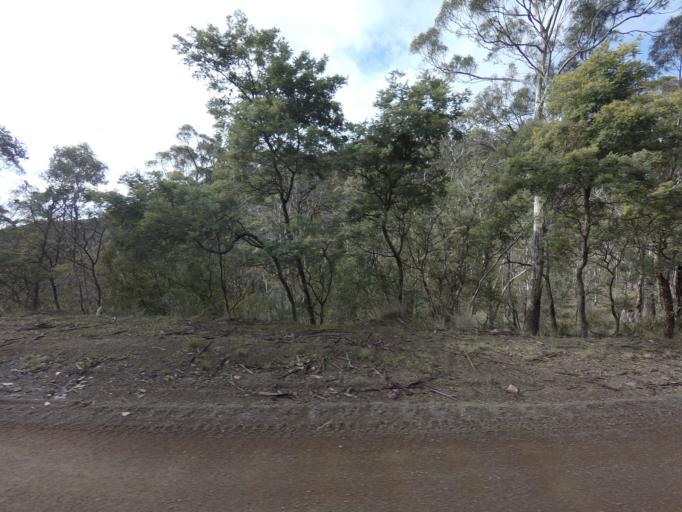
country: AU
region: Tasmania
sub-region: Derwent Valley
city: New Norfolk
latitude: -42.7441
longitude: 146.8673
